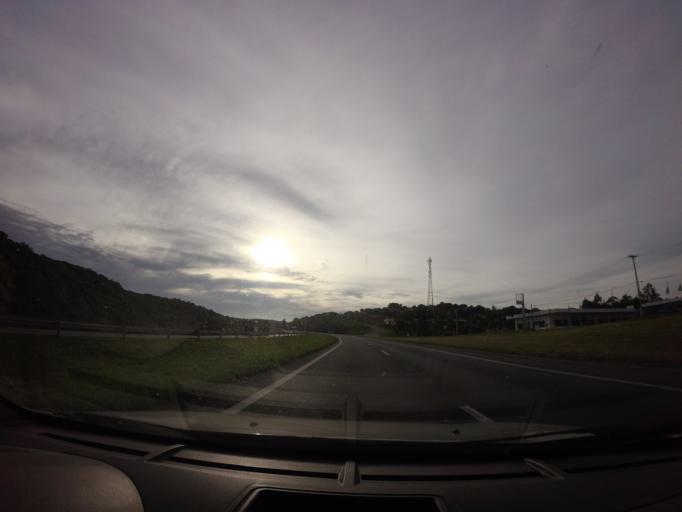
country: BR
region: Sao Paulo
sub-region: Jarinu
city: Jarinu
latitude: -23.0282
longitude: -46.7483
